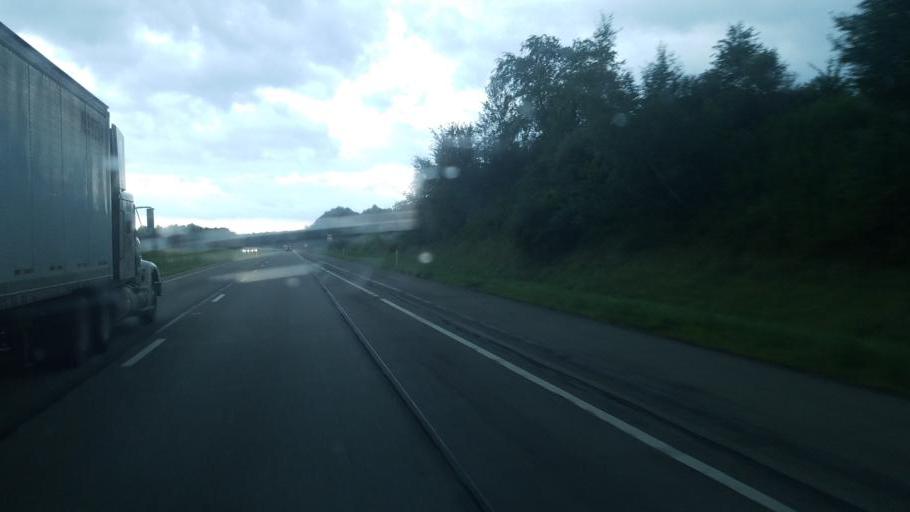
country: US
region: Pennsylvania
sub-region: Mercer County
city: Grove City
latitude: 41.0958
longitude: -80.1414
